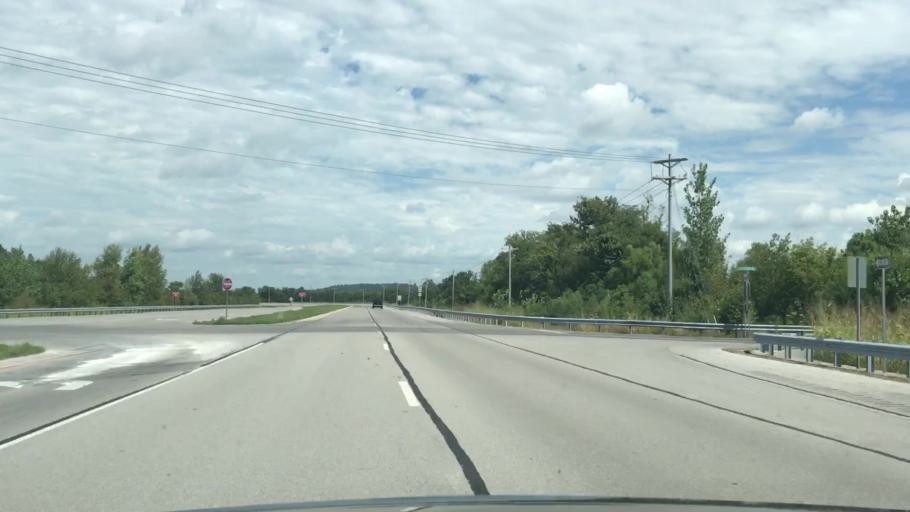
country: US
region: Kentucky
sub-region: Logan County
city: Russellville
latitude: 36.8550
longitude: -86.8627
